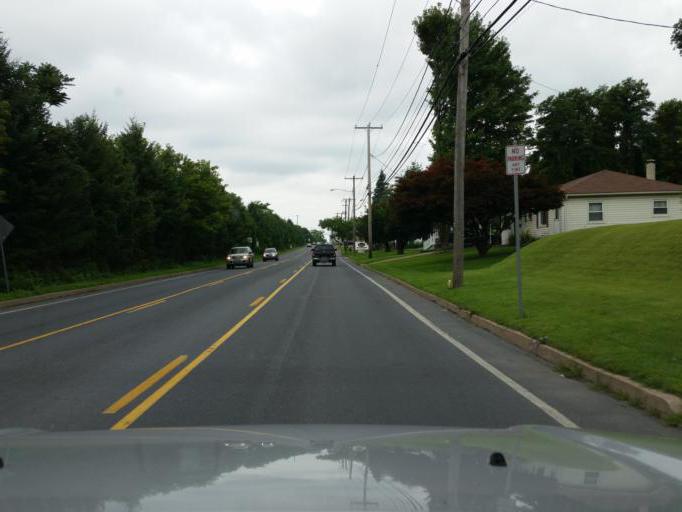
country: US
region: Pennsylvania
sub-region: Dauphin County
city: Rutherford
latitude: 40.2646
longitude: -76.7729
